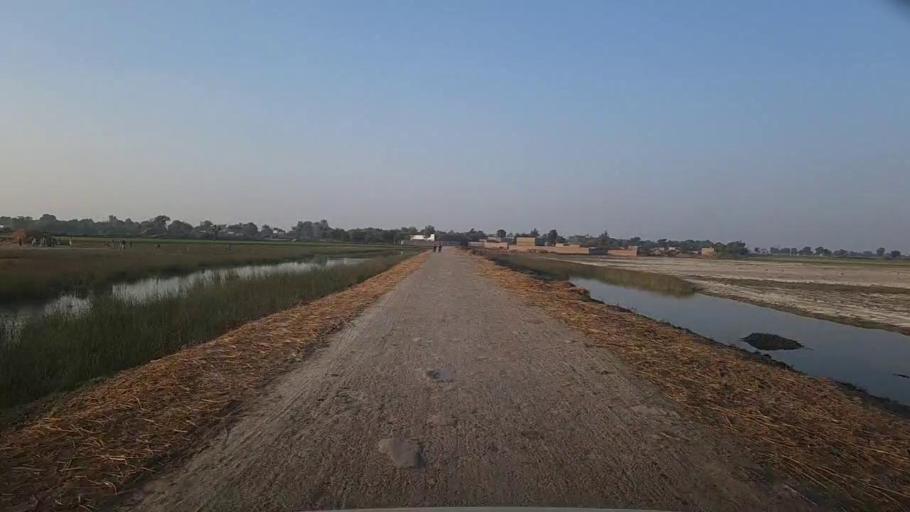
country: PK
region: Sindh
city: Mehar
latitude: 27.1956
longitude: 67.7822
